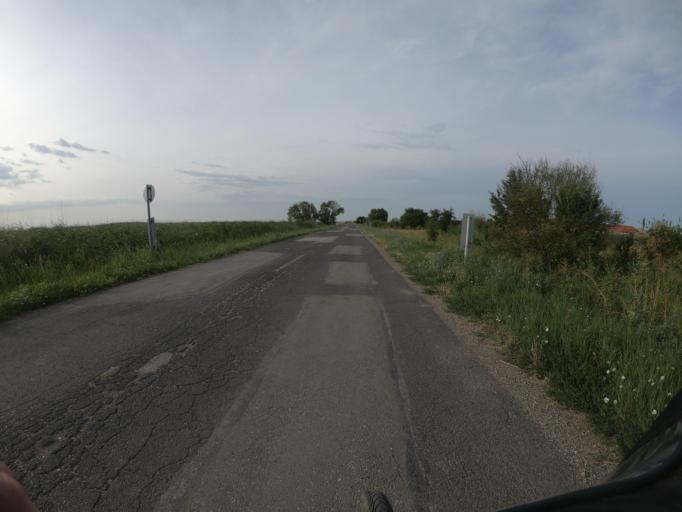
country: HU
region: Hajdu-Bihar
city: Hortobagy
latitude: 47.6032
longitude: 21.0759
